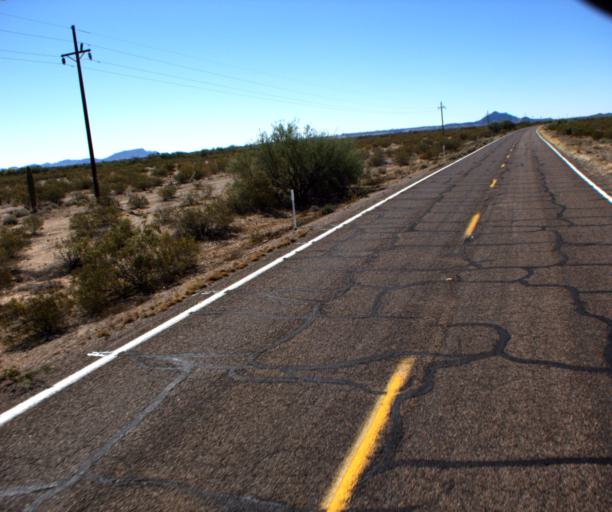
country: US
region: Arizona
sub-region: Pima County
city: Ajo
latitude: 32.4556
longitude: -112.8720
